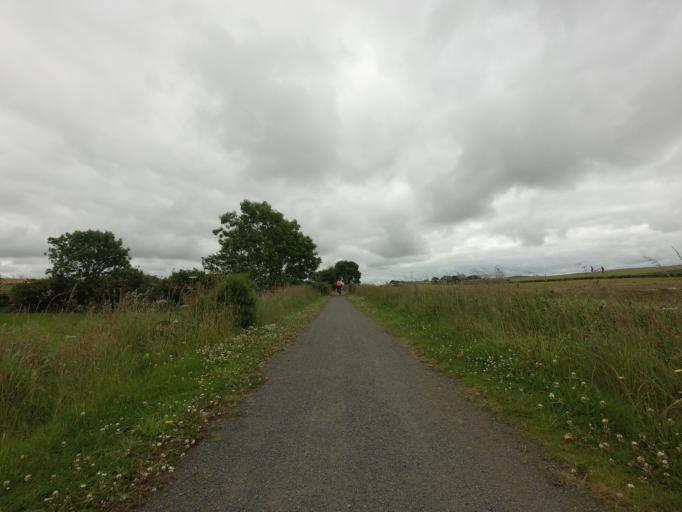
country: GB
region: Scotland
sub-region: Aberdeenshire
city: Ellon
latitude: 57.4738
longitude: -2.1254
